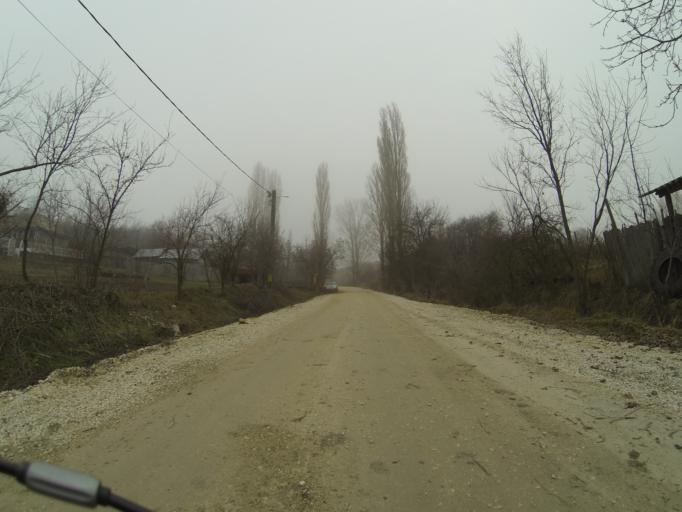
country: RO
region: Mehedinti
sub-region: Comuna Balacita
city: Gvardinita
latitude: 44.4094
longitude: 23.1434
